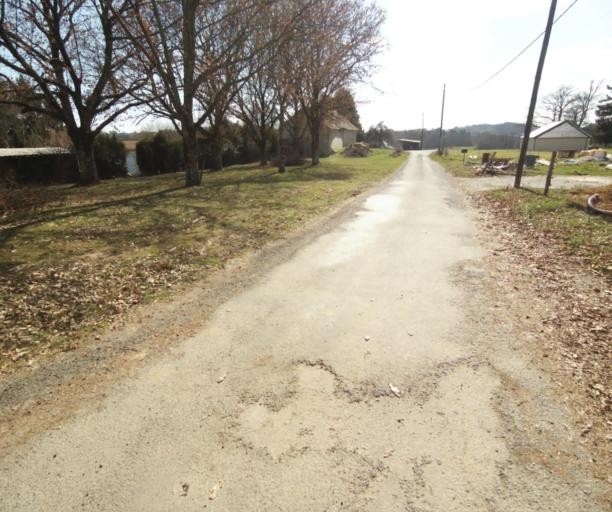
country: FR
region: Limousin
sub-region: Departement de la Correze
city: Saint-Mexant
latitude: 45.3024
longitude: 1.6610
